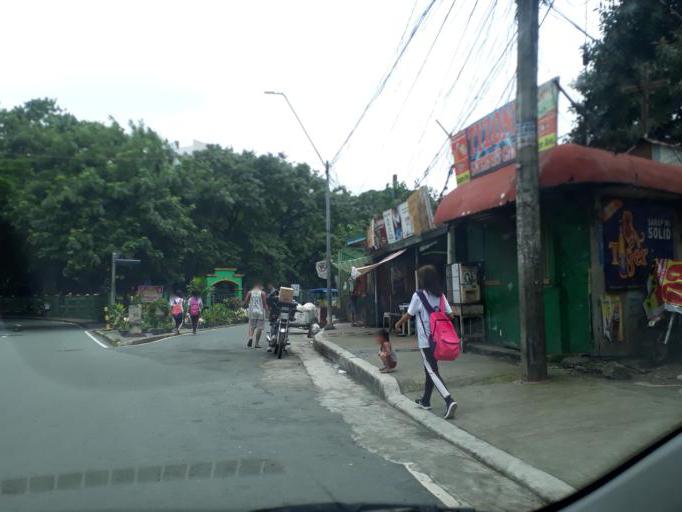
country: PH
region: Calabarzon
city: Del Monte
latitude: 14.6320
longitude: 121.0209
